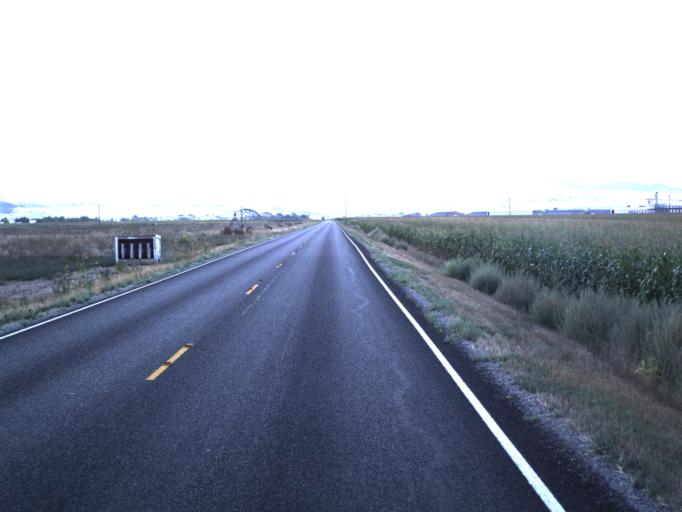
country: US
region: Utah
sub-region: Cache County
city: Lewiston
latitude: 41.9249
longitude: -111.8882
